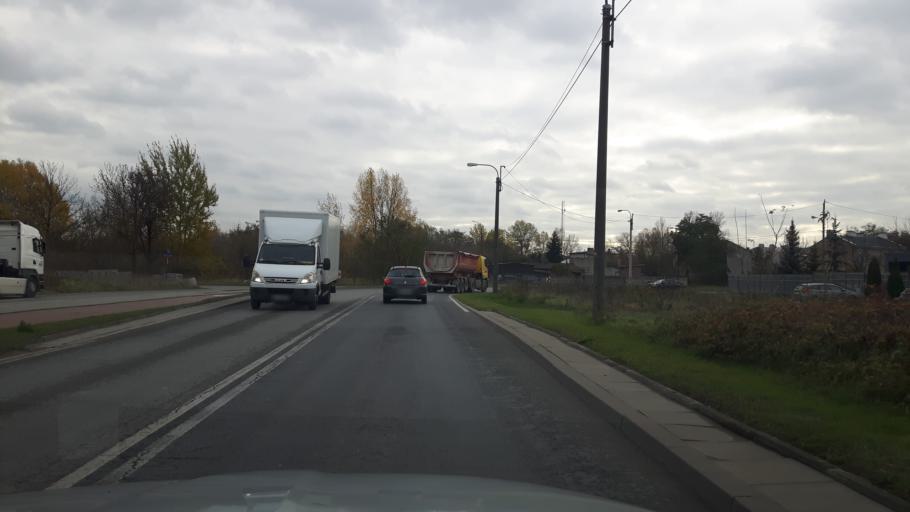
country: PL
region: Masovian Voivodeship
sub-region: Warszawa
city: Praga Poludnie
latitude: 52.2629
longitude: 21.0783
